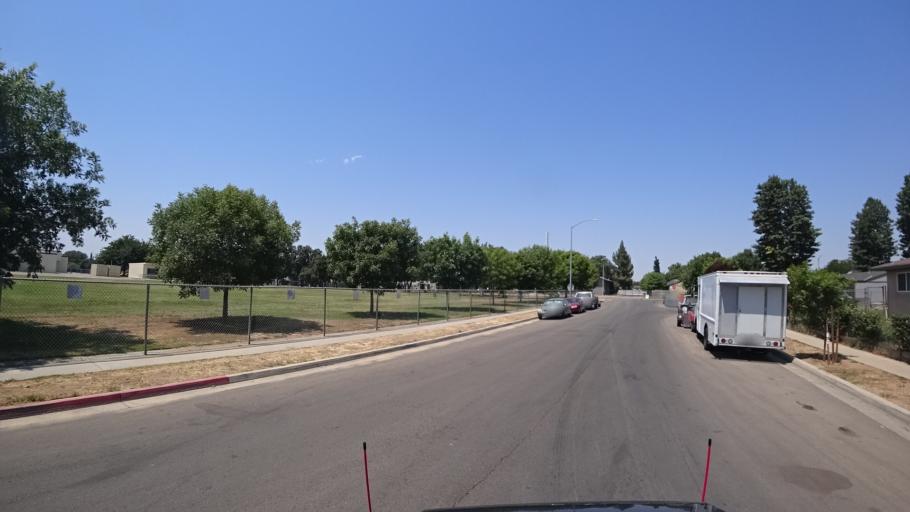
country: US
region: California
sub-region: Fresno County
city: Fresno
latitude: 36.7197
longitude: -119.7989
